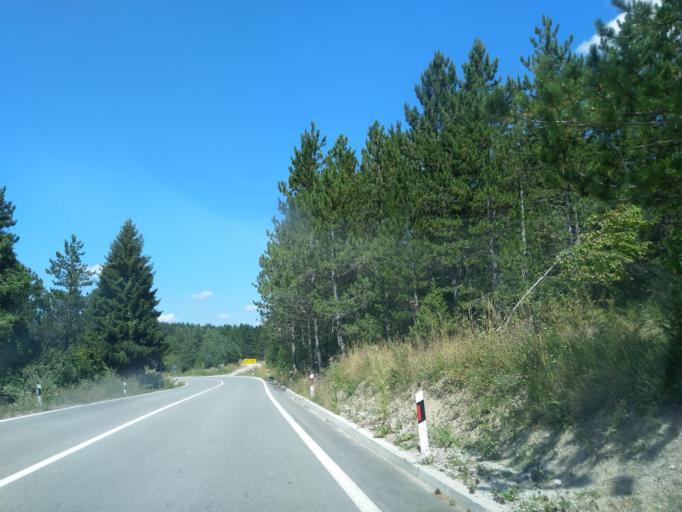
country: RS
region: Central Serbia
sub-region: Zlatiborski Okrug
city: Sjenica
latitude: 43.3102
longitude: 19.8979
